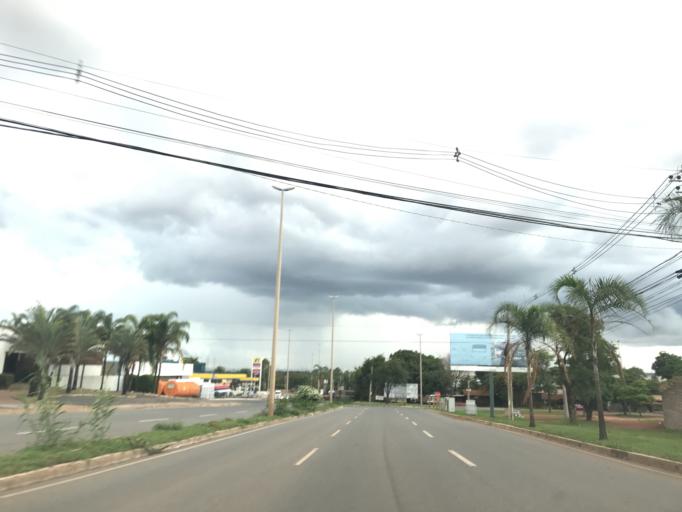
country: BR
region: Federal District
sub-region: Brasilia
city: Brasilia
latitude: -15.8000
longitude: -47.9713
